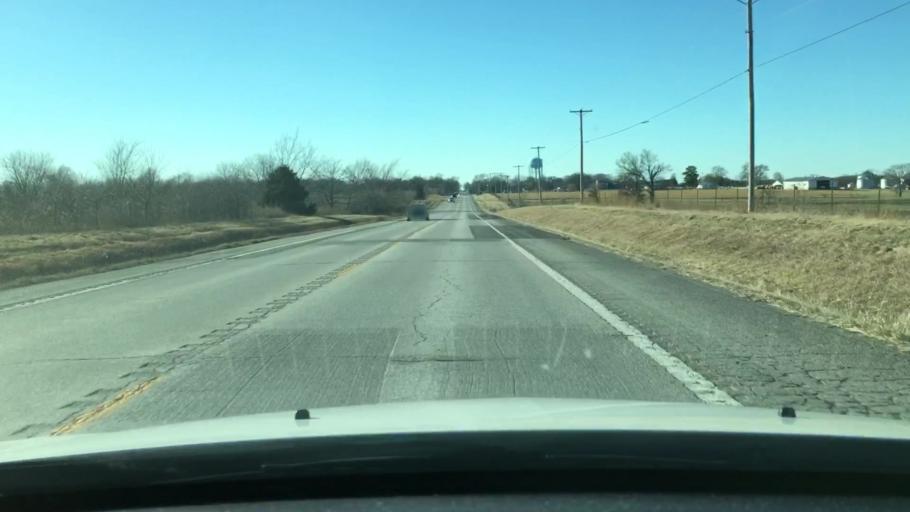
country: US
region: Missouri
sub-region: Pike County
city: Bowling Green
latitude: 39.3451
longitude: -91.3267
